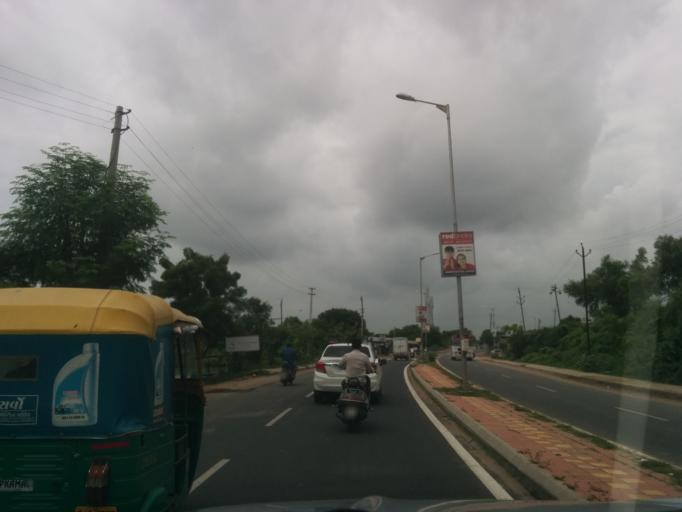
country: IN
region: Gujarat
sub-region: Ahmadabad
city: Sarkhej
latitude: 23.0525
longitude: 72.4746
